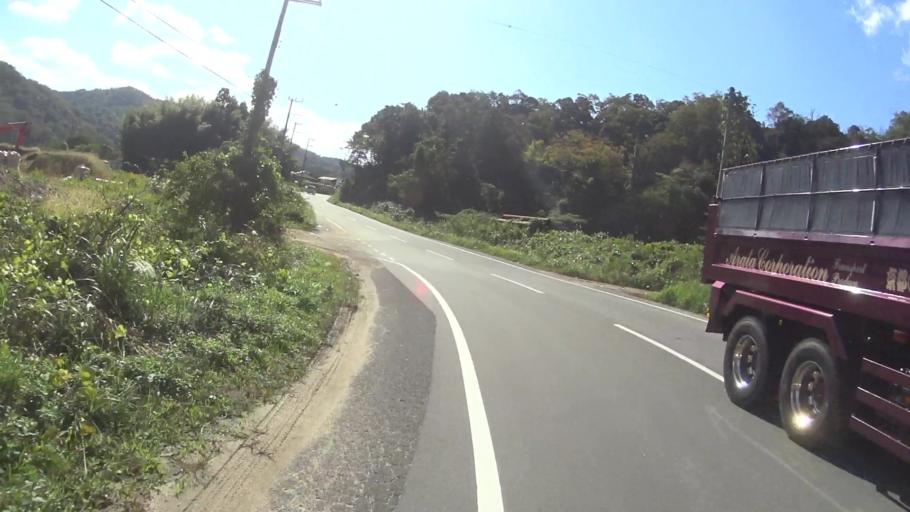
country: JP
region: Kyoto
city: Miyazu
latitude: 35.6989
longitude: 135.1013
